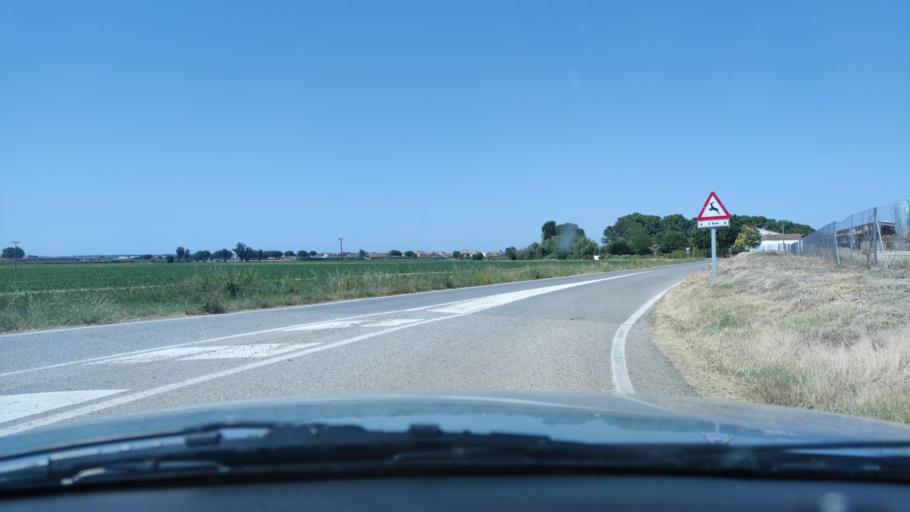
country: ES
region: Catalonia
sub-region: Provincia de Lleida
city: Mollerussa
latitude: 41.6584
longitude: 0.8958
